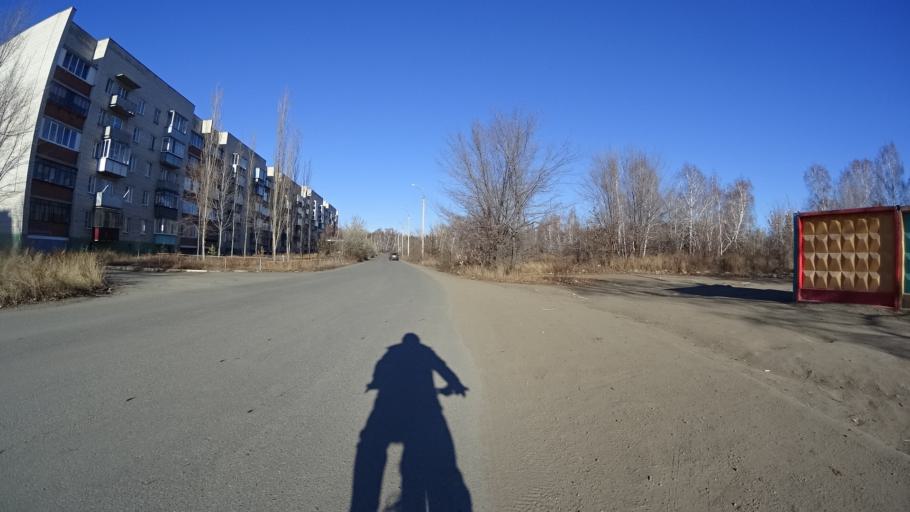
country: RU
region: Chelyabinsk
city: Troitsk
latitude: 54.0515
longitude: 61.6406
